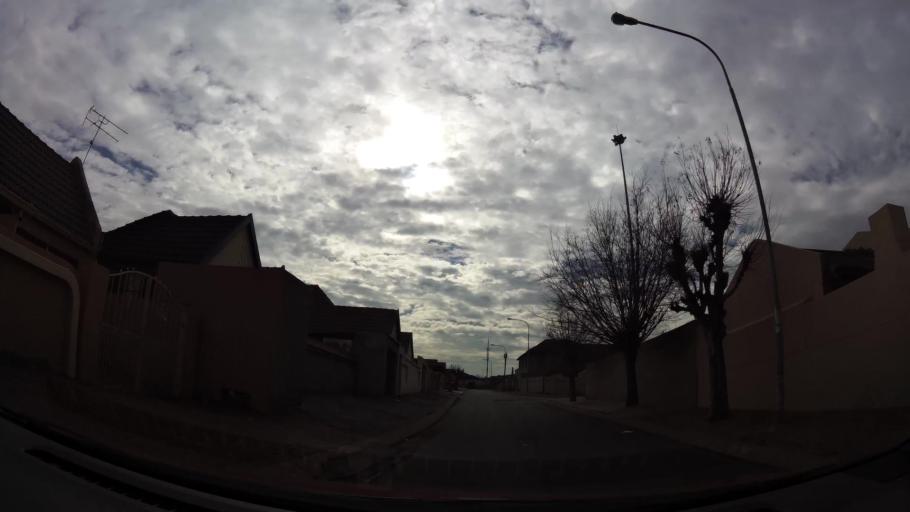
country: ZA
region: Gauteng
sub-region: City of Johannesburg Metropolitan Municipality
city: Soweto
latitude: -26.2777
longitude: 27.8321
